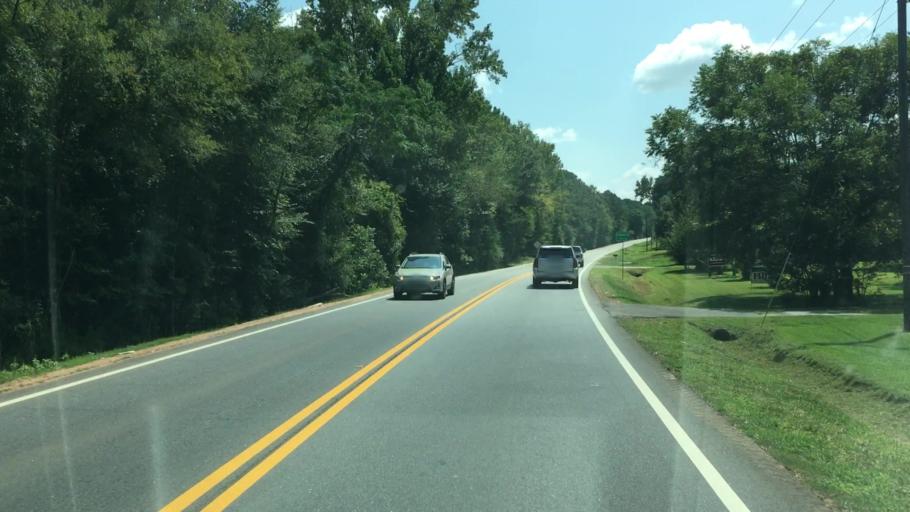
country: US
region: Georgia
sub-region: Oconee County
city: Watkinsville
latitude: 33.7843
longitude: -83.4230
